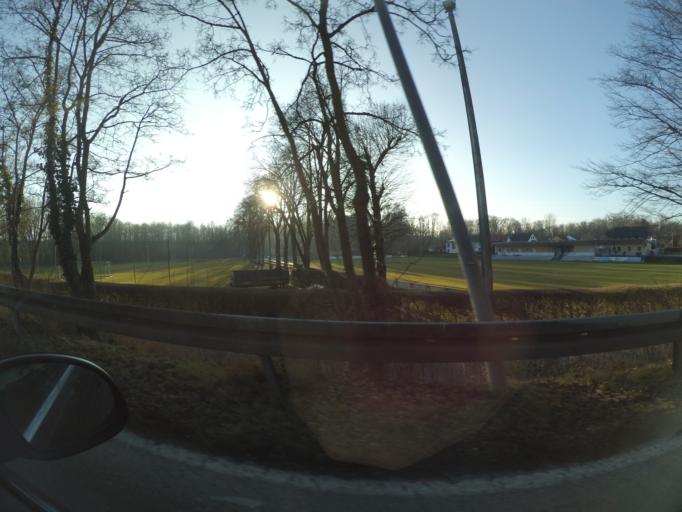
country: DE
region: Bavaria
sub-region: Swabia
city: Leipheim
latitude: 48.4531
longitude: 10.2135
